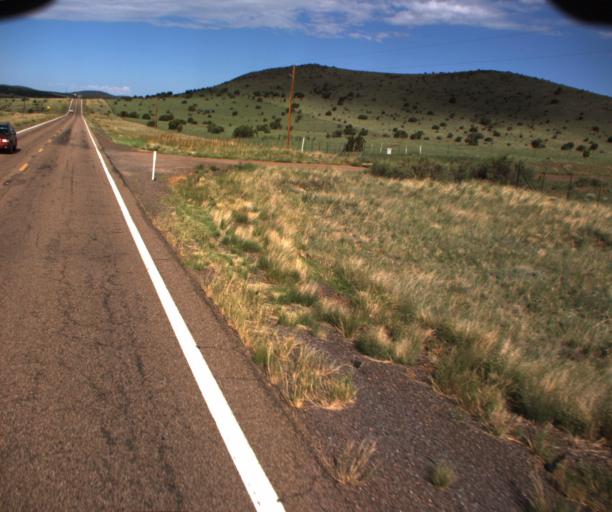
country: US
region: Arizona
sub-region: Navajo County
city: Pinetop-Lakeside
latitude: 34.2704
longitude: -109.6394
